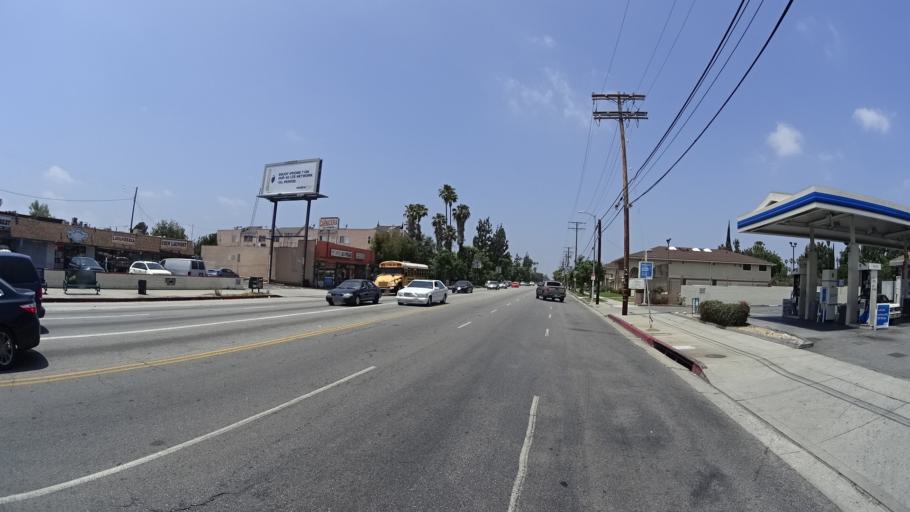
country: US
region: California
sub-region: Los Angeles County
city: Van Nuys
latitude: 34.1867
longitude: -118.4576
